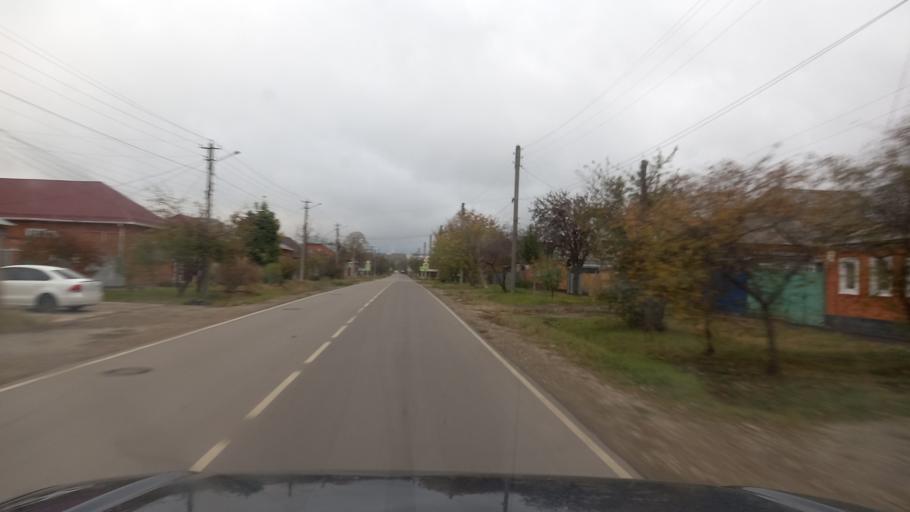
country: RU
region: Adygeya
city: Maykop
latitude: 44.6107
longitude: 40.1227
